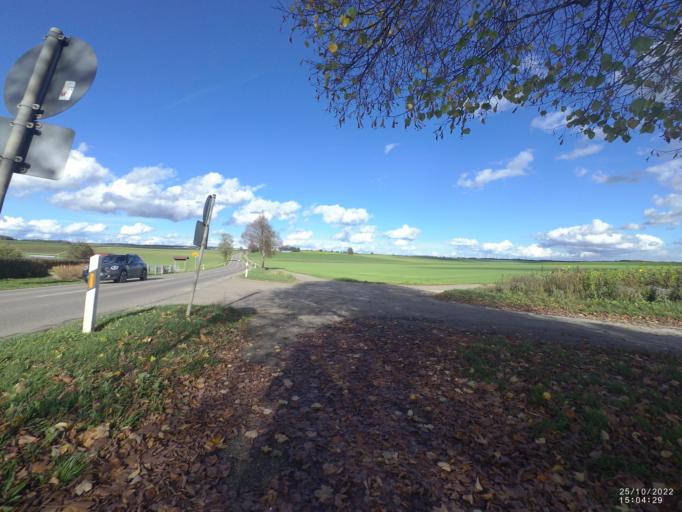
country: DE
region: Baden-Wuerttemberg
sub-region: Regierungsbezirk Stuttgart
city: Bohmenkirch
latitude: 48.6657
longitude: 9.9137
